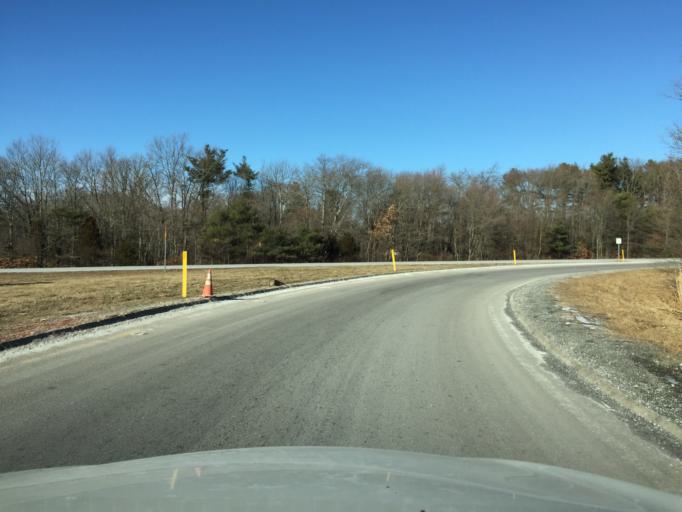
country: US
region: Massachusetts
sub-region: Bristol County
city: Mansfield Center
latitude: 42.0245
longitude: -71.2580
